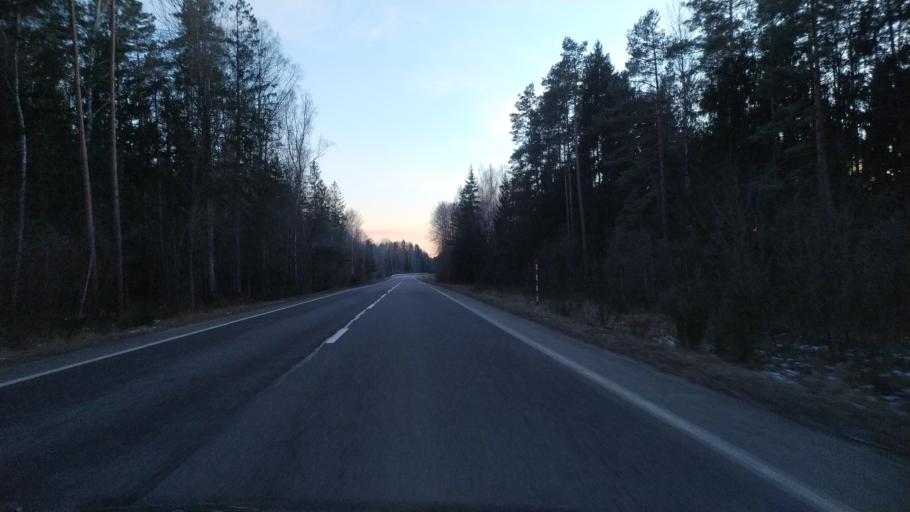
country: BY
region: Brest
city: Pruzhany
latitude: 52.5048
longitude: 24.1764
